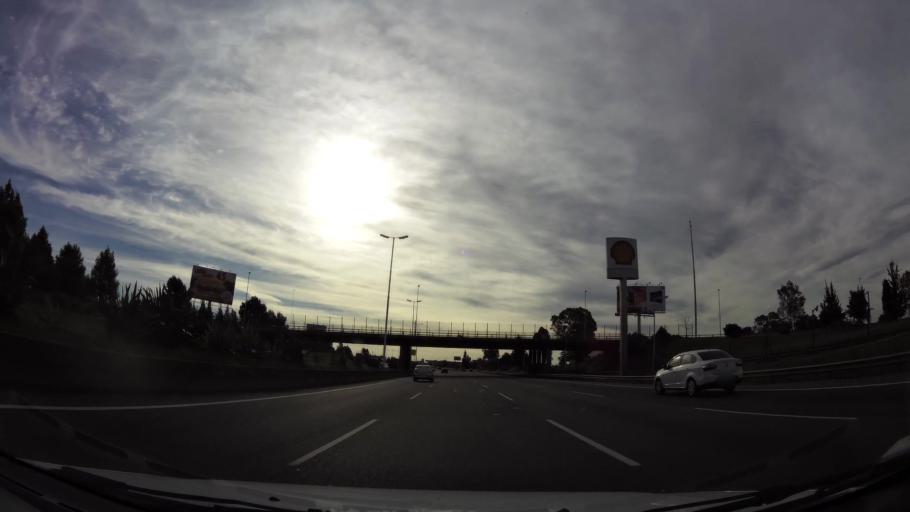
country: AR
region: Buenos Aires
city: Caseros
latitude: -34.6297
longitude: -58.5531
